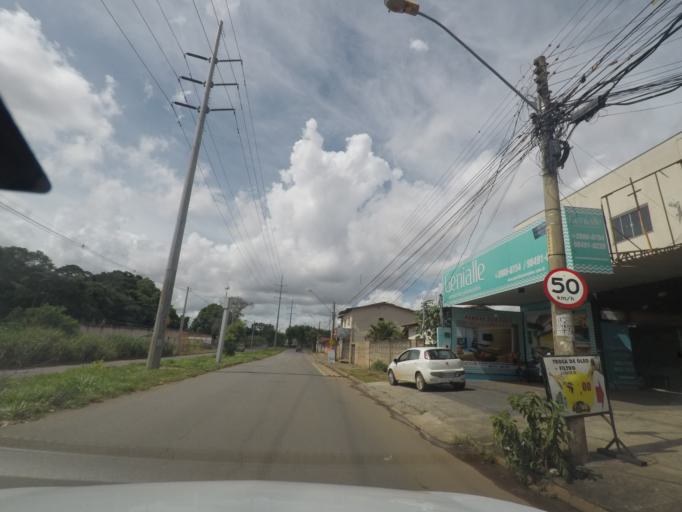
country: BR
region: Goias
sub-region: Goiania
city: Goiania
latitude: -16.7205
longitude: -49.3359
